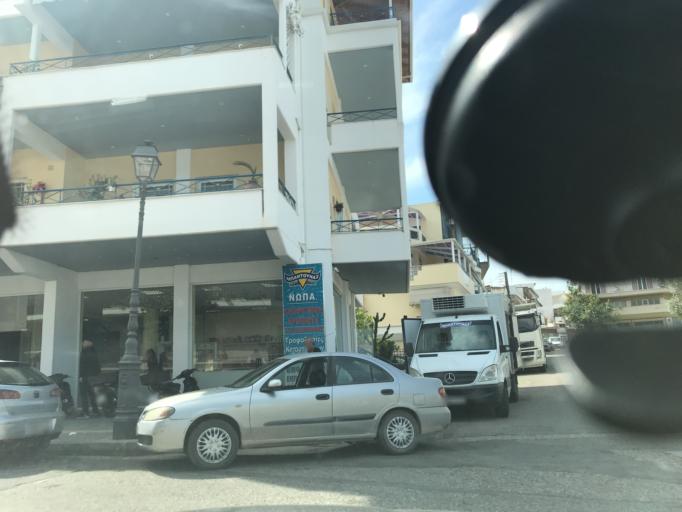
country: GR
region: West Greece
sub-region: Nomos Ileias
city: Pyrgos
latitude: 37.6746
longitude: 21.4450
